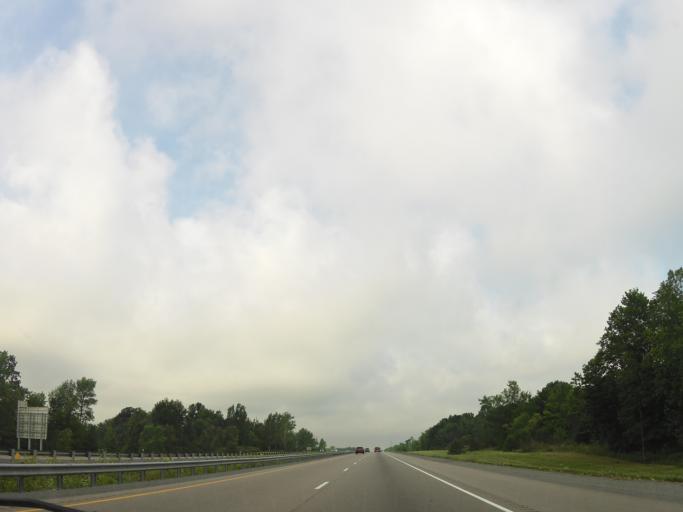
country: CA
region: Ontario
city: Skatepark
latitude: 44.2818
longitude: -76.7319
